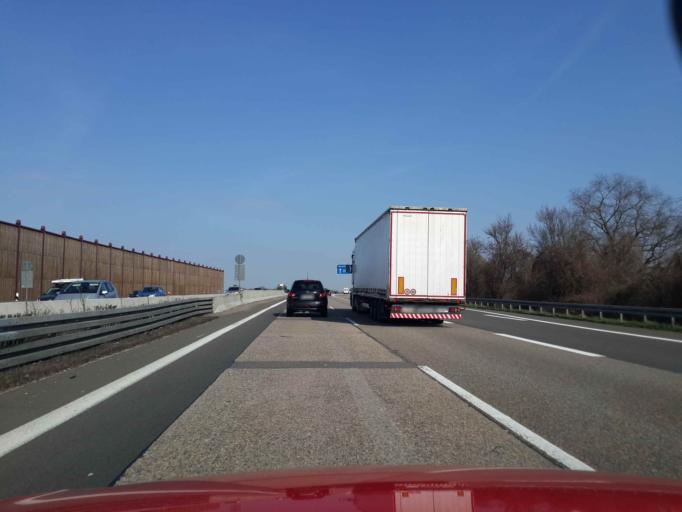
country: DE
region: Baden-Wuerttemberg
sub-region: Karlsruhe Region
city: Eppelheim
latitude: 49.4101
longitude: 8.6355
